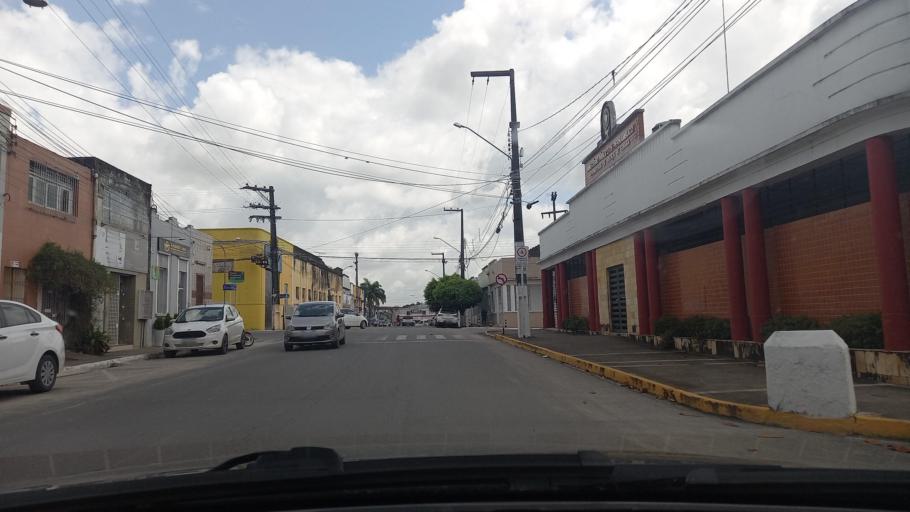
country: BR
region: Pernambuco
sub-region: Goiana
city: Goiana
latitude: -7.5585
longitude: -34.9964
